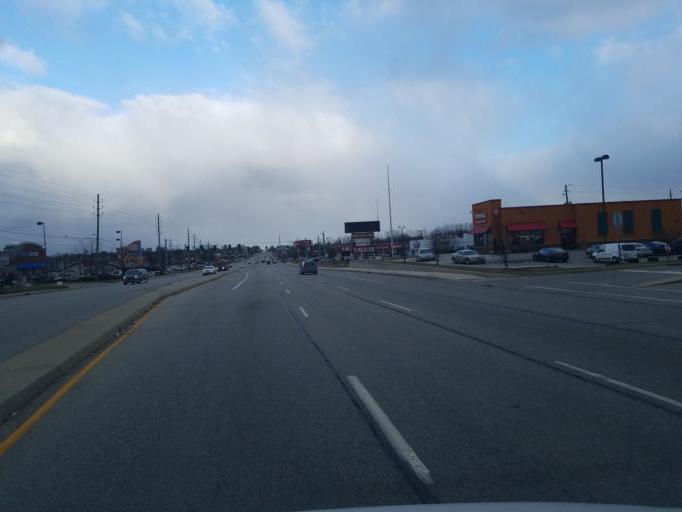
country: US
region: Indiana
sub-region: Marion County
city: Cumberland
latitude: 39.7749
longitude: -85.9895
